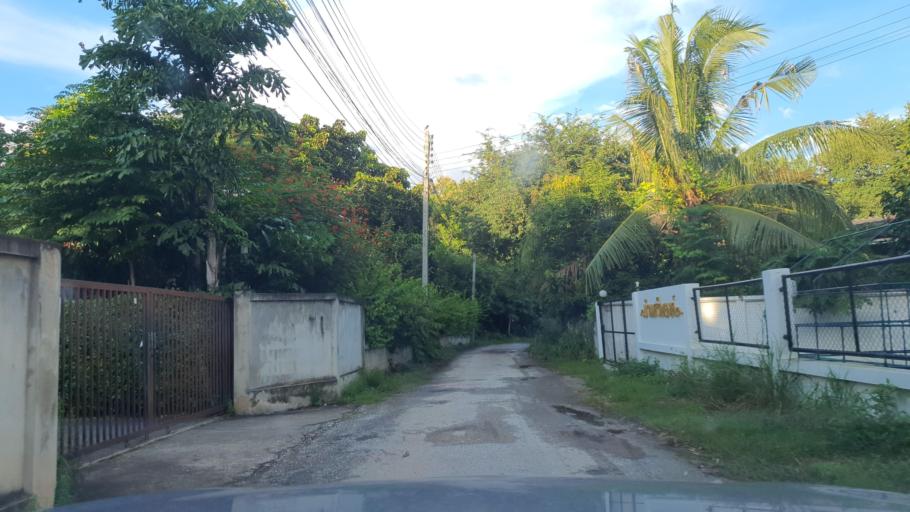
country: TH
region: Chiang Mai
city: Chiang Mai
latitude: 18.7731
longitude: 98.9451
